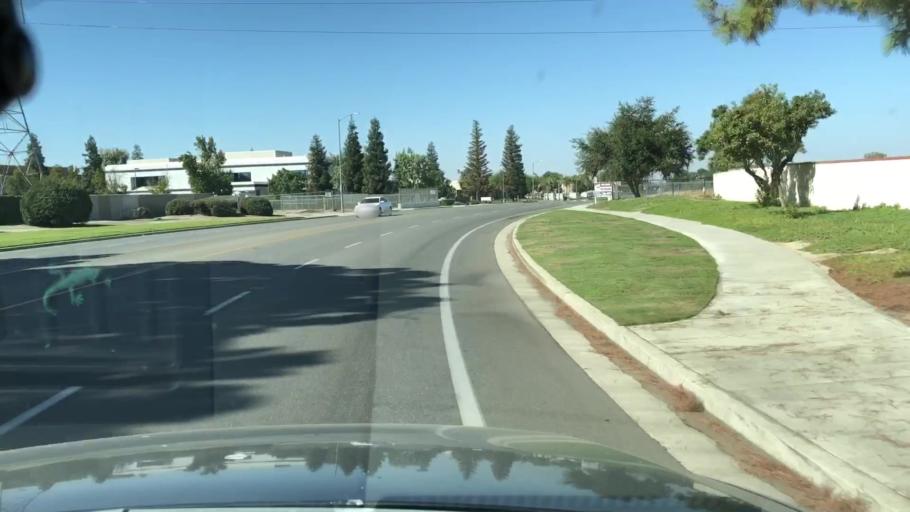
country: US
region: California
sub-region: Kern County
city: Greenacres
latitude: 35.3430
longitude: -119.0957
